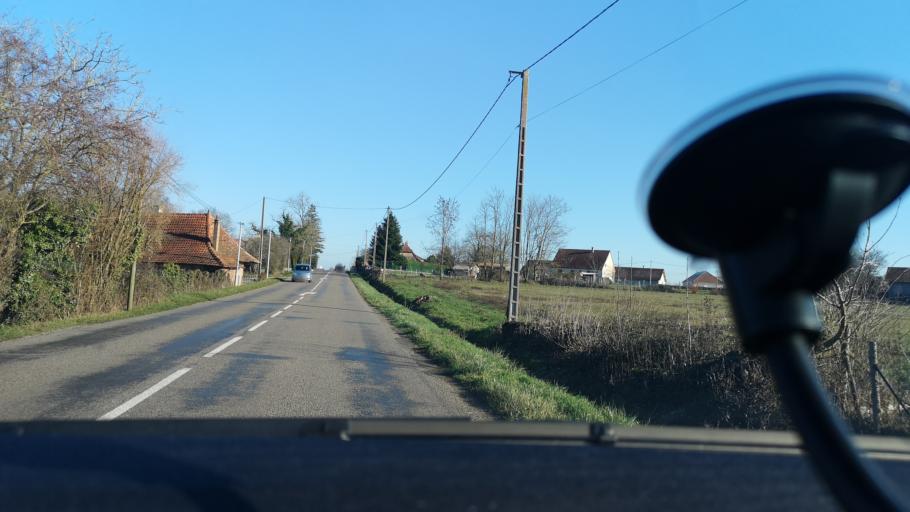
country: FR
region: Bourgogne
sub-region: Departement de Saone-et-Loire
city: Saint-Germain-du-Bois
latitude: 46.7490
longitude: 5.2208
